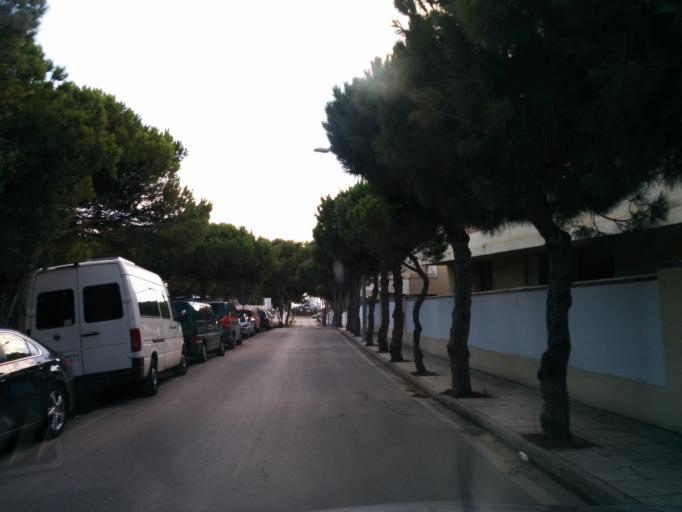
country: ES
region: Andalusia
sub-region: Provincia de Cadiz
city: Vejer de la Frontera
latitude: 36.1868
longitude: -6.0083
